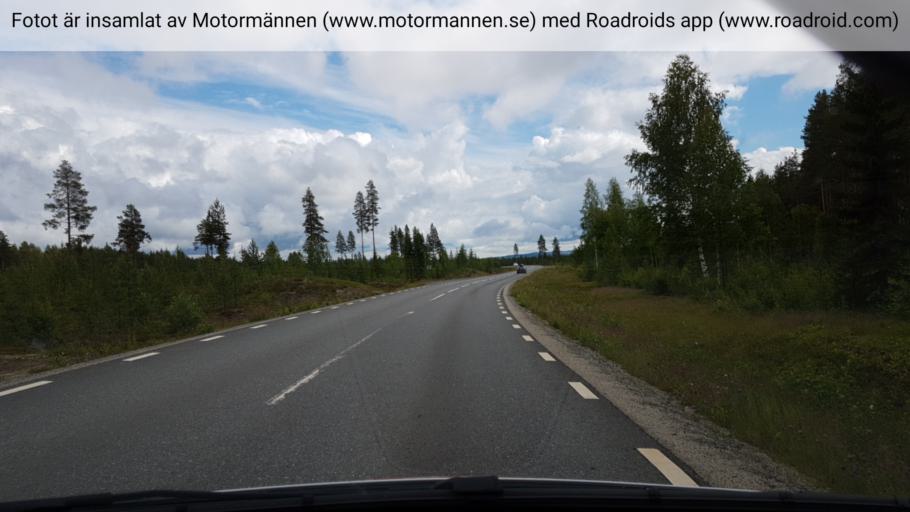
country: SE
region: Vaesterbotten
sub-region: Lycksele Kommun
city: Lycksele
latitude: 64.3951
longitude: 19.0713
